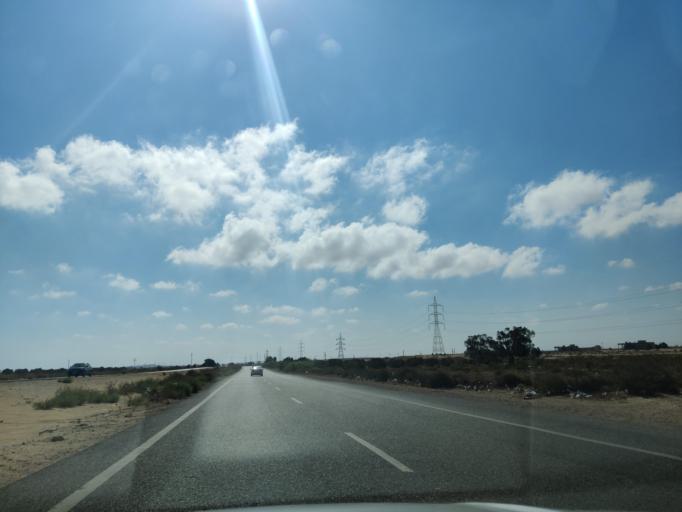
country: EG
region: Muhafazat Matruh
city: Al `Alamayn
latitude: 31.0541
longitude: 28.2858
